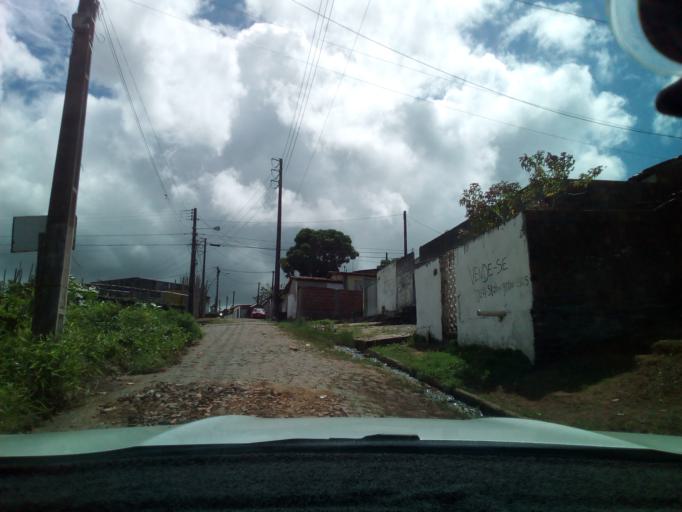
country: BR
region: Paraiba
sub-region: Bayeux
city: Bayeux
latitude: -7.1353
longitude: -34.9352
